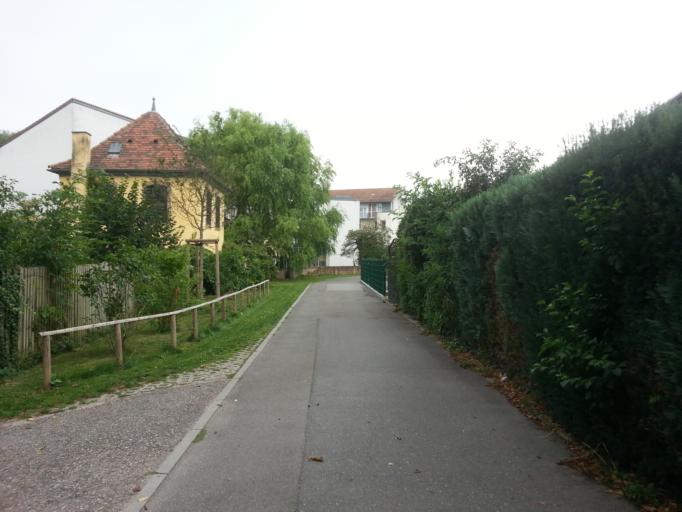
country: DE
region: Baden-Wuerttemberg
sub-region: Karlsruhe Region
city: Ladenburg
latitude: 49.4721
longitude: 8.6158
